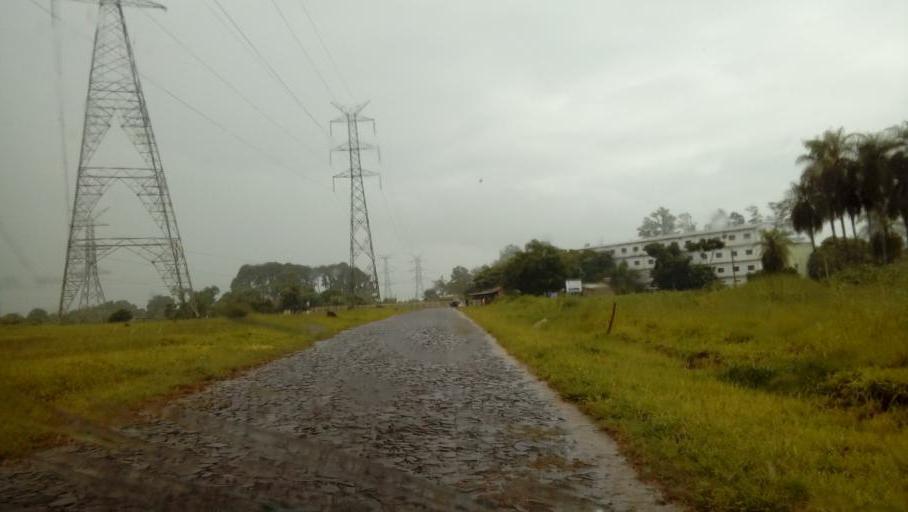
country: PY
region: Alto Parana
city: Ciudad del Este
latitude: -25.4275
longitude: -54.6405
